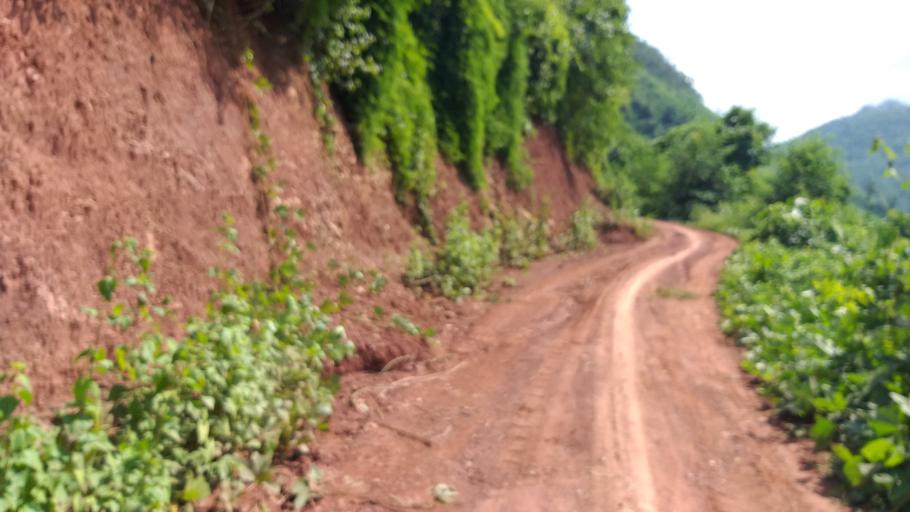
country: LA
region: Phongsali
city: Khoa
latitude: 21.3029
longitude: 102.5496
